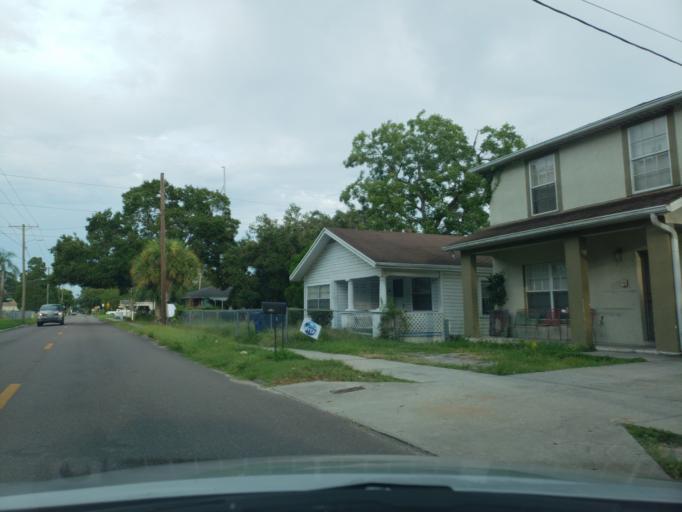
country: US
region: Florida
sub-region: Hillsborough County
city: Tampa
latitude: 27.9703
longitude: -82.4326
